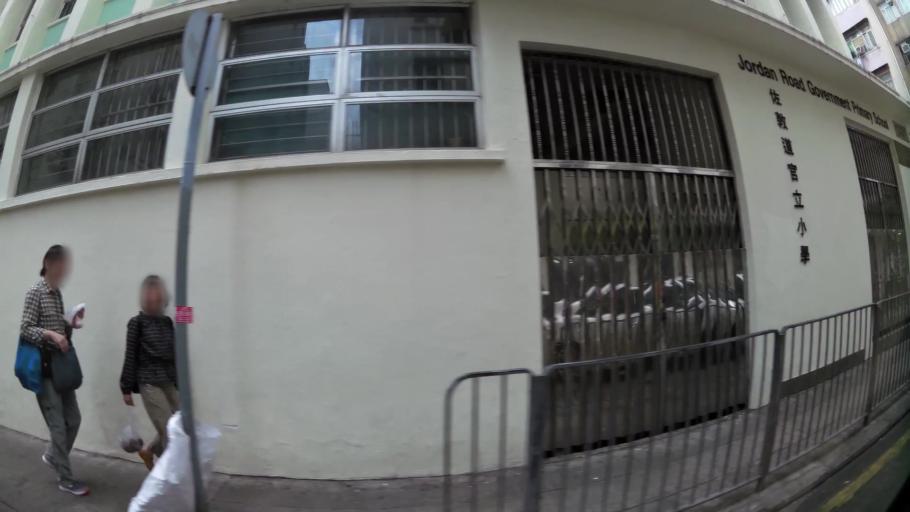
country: HK
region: Kowloon City
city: Kowloon
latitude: 22.3063
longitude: 114.1689
